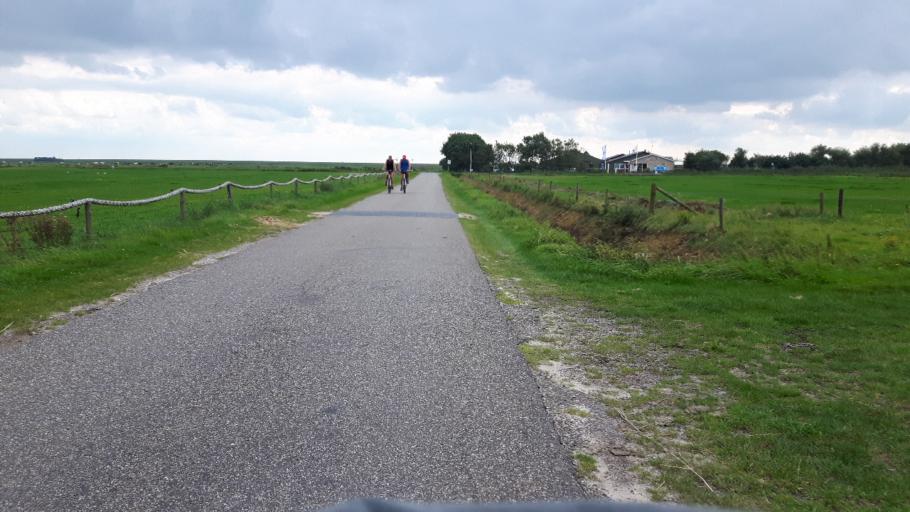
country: NL
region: Friesland
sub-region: Gemeente Ameland
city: Nes
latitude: 53.4510
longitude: 5.8180
